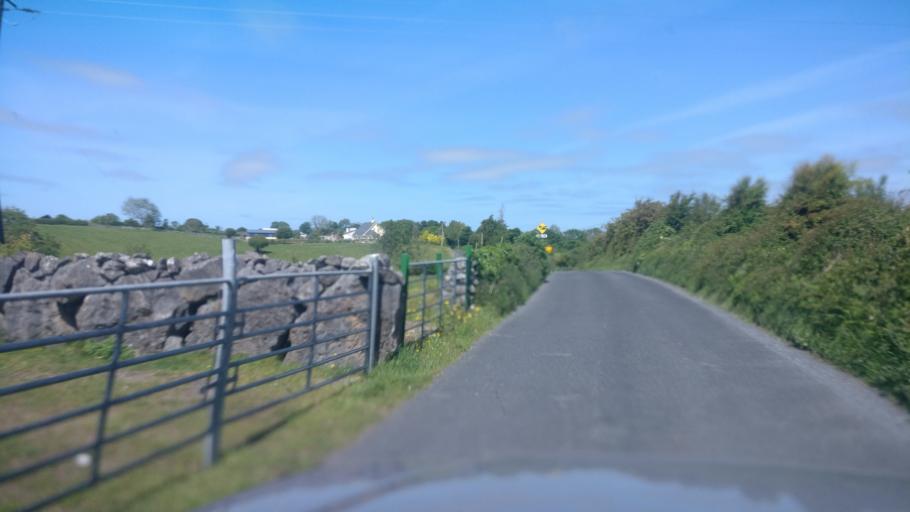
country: IE
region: Connaught
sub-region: County Galway
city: Gort
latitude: 53.0925
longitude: -8.8070
